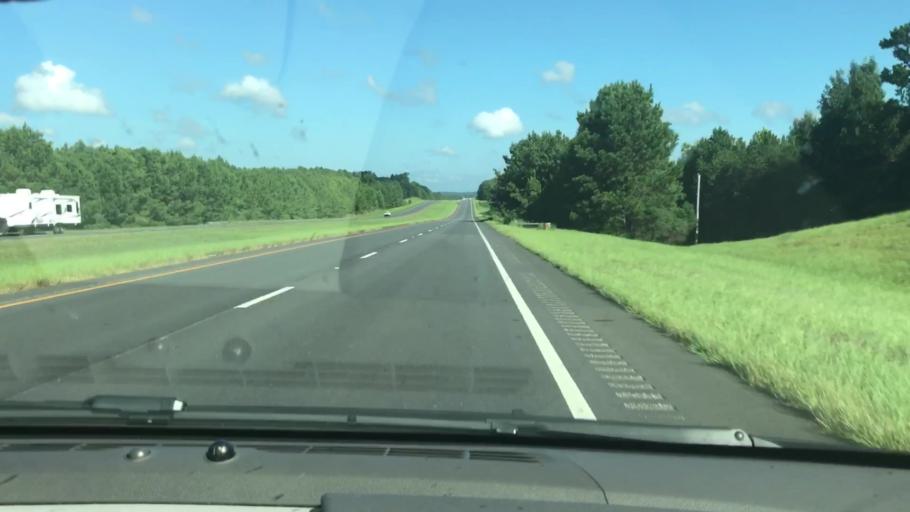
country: US
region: Alabama
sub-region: Barbour County
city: Eufaula
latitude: 32.0404
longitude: -85.1275
